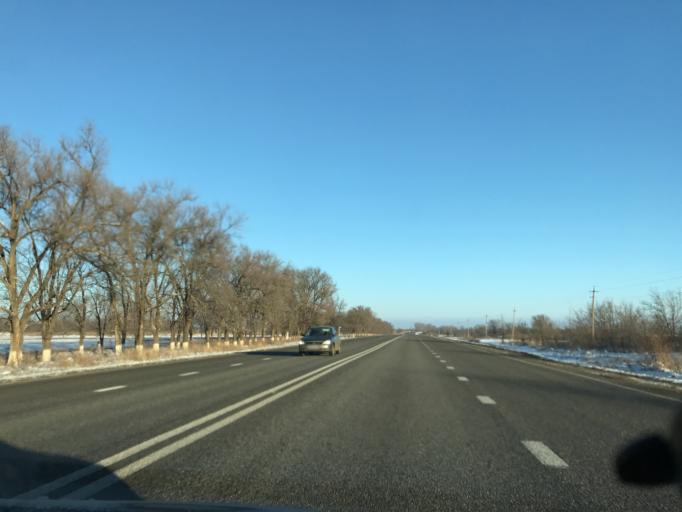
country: RU
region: Stavropol'skiy
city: Bezopasnoye
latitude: 45.5929
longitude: 41.9438
